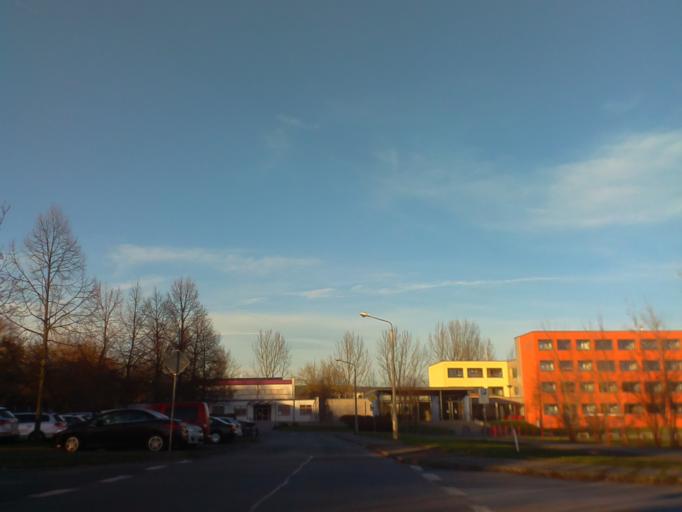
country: DE
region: Thuringia
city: Rudolstadt
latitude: 50.6946
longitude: 11.3236
